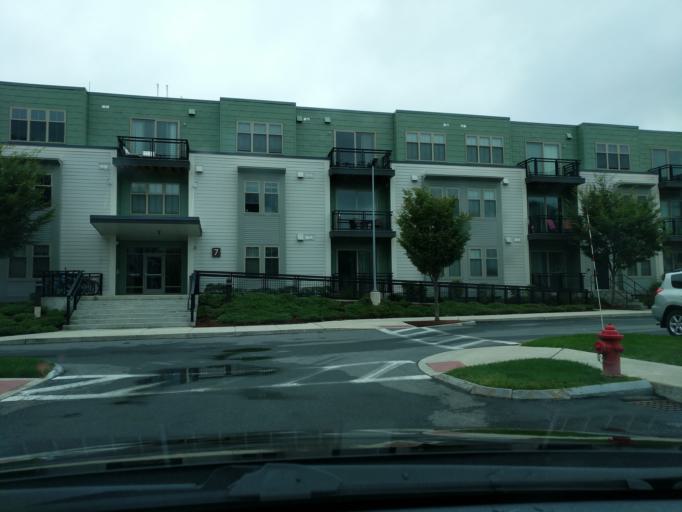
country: US
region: Massachusetts
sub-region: Middlesex County
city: Somerville
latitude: 42.3936
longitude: -71.1076
